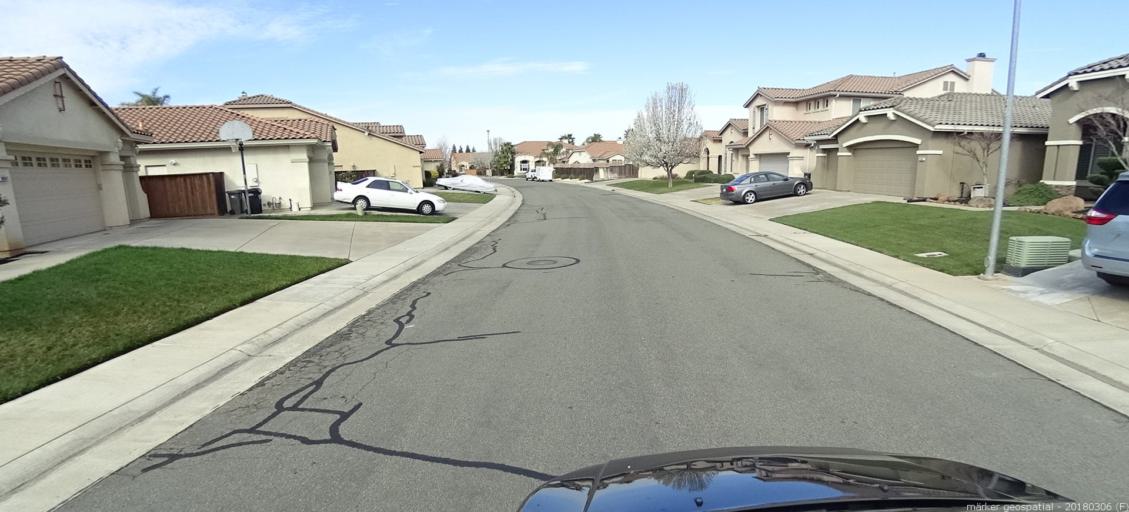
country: US
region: California
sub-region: Sacramento County
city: Vineyard
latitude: 38.4699
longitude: -121.3176
